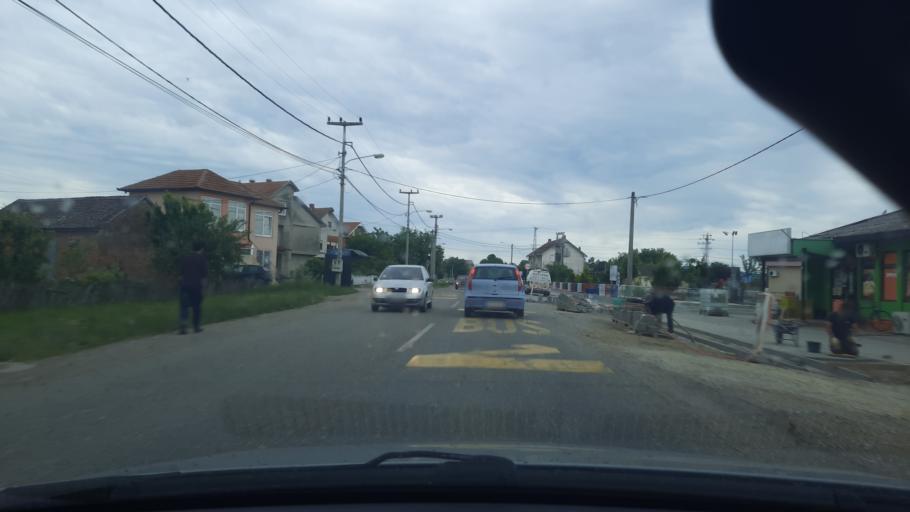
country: RS
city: Jevremovac
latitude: 44.7220
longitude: 19.6640
